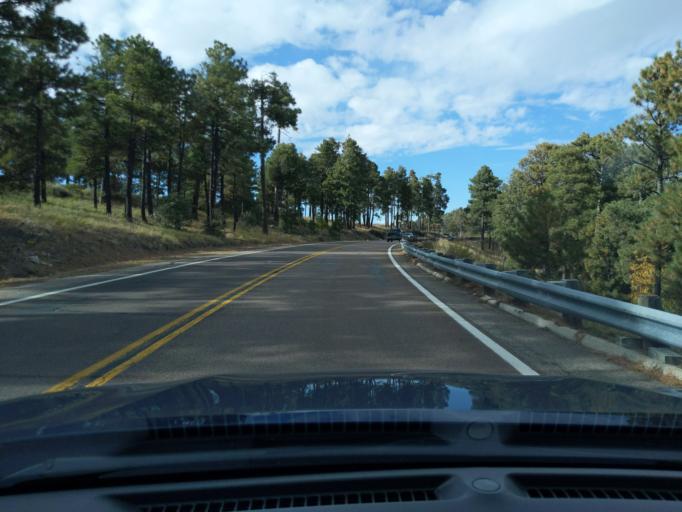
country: US
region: Arizona
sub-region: Pinal County
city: Oracle
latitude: 32.4338
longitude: -110.7517
